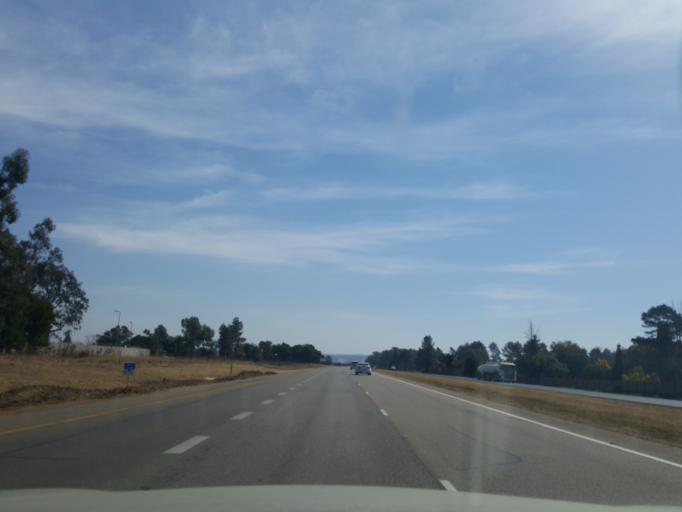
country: ZA
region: Gauteng
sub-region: City of Tshwane Metropolitan Municipality
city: Bronkhorstspruit
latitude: -25.8192
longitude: 28.7427
